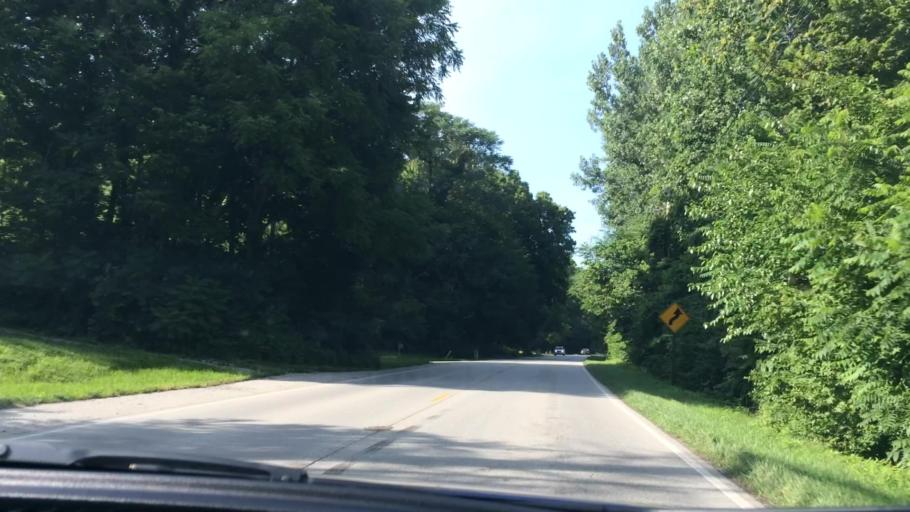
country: US
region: Indiana
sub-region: Tippecanoe County
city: West Lafayette
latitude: 40.4469
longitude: -86.8962
